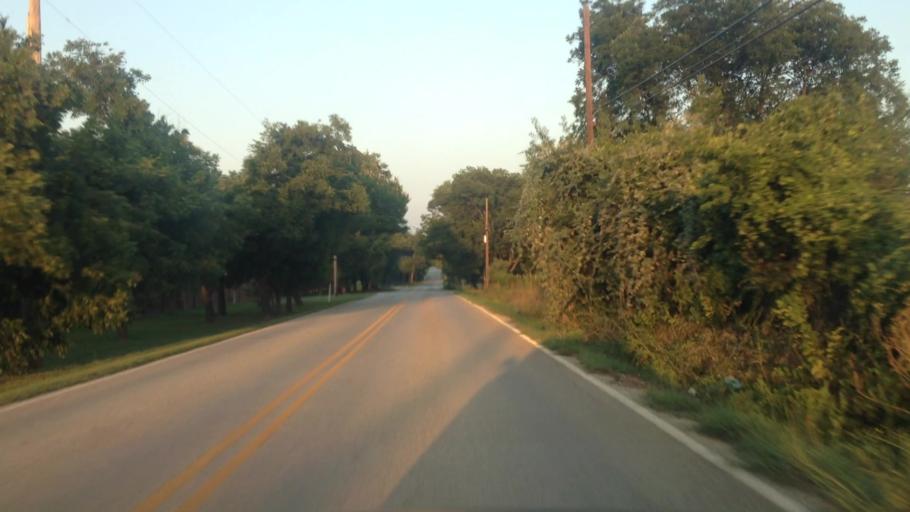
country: US
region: Texas
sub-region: Tarrant County
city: Kennedale
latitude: 32.6333
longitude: -97.1986
